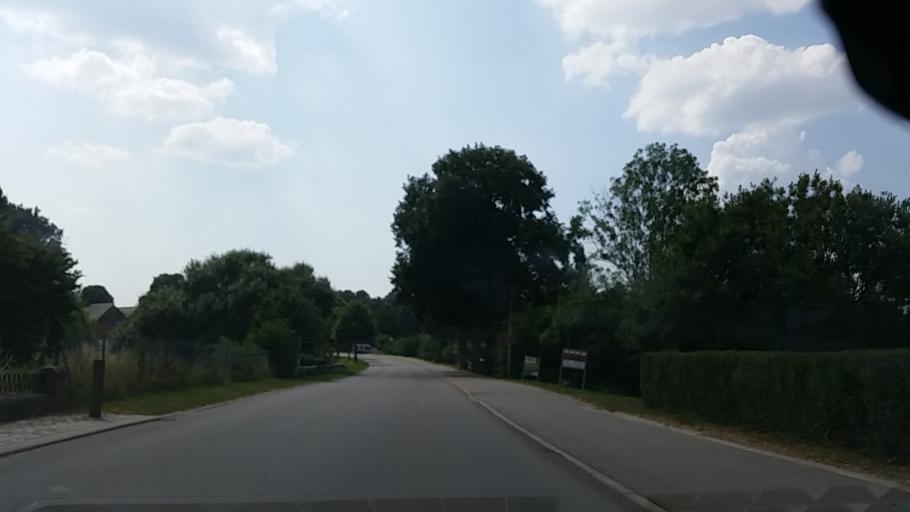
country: DE
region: Schleswig-Holstein
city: Alt Molln
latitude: 53.6218
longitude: 10.6612
